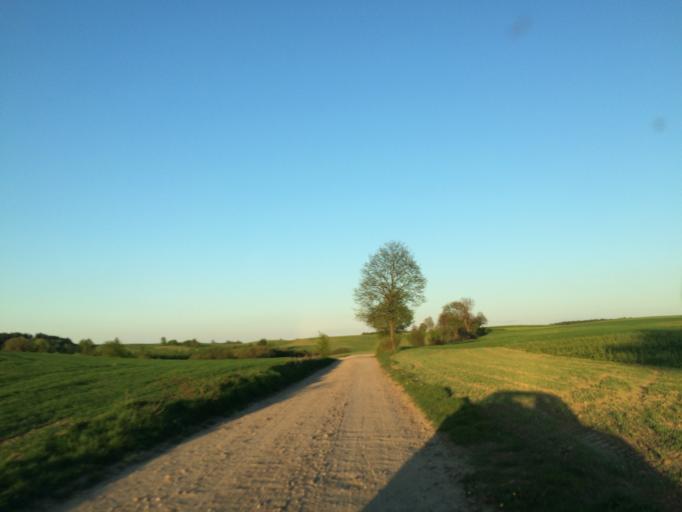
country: PL
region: Warmian-Masurian Voivodeship
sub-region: Powiat dzialdowski
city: Rybno
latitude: 53.4749
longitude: 19.8800
